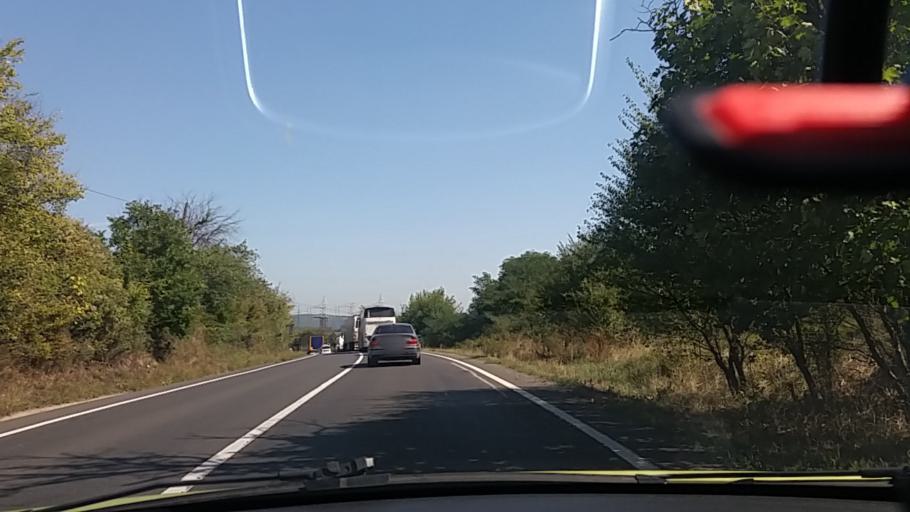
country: RO
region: Hunedoara
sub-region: Comuna Dobra
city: Dobra
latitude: 45.9397
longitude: 22.5632
